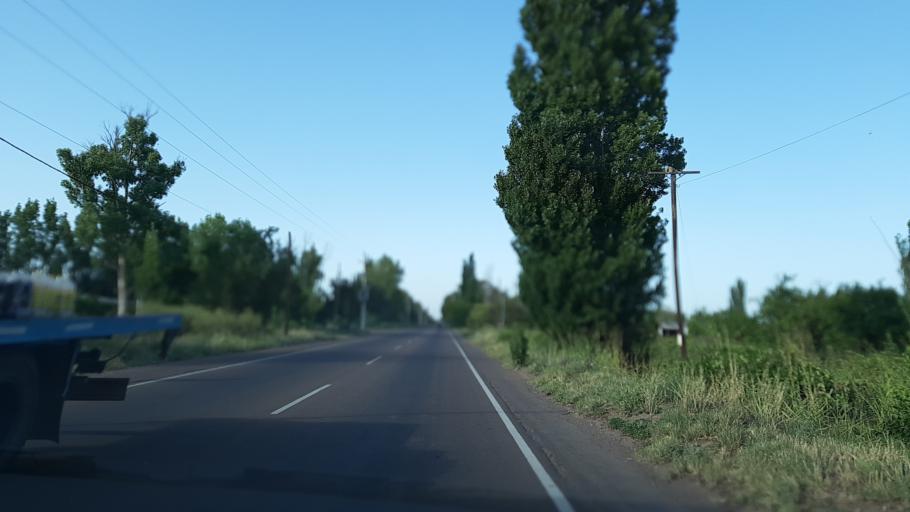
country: AR
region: Mendoza
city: San Martin
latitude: -32.9738
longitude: -68.4526
